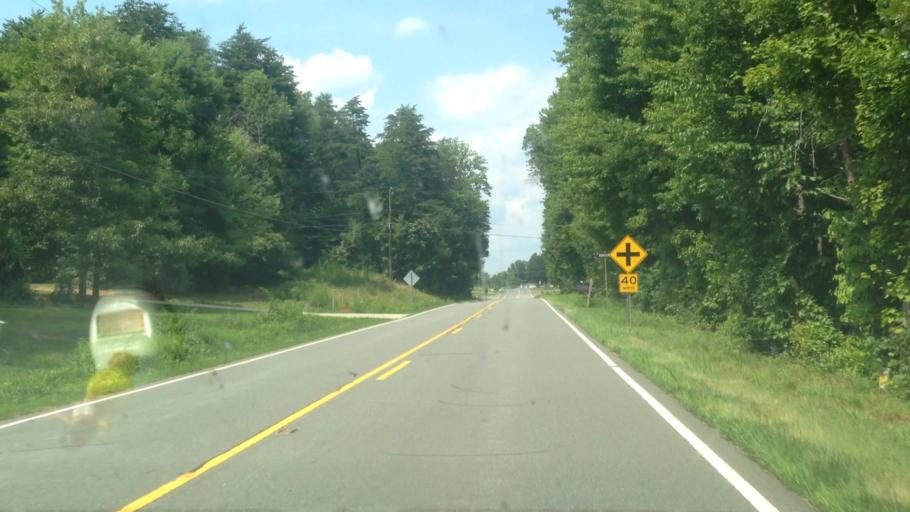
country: US
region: North Carolina
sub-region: Stokes County
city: Danbury
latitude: 36.4001
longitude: -80.0947
